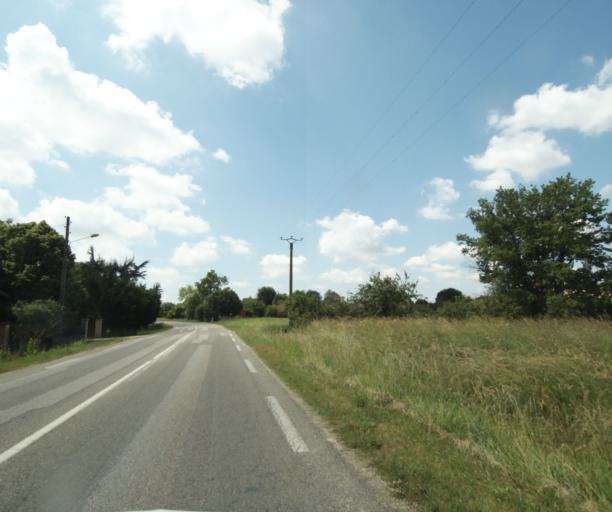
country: FR
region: Midi-Pyrenees
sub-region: Departement du Tarn-et-Garonne
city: Montauban
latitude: 44.0558
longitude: 1.3591
